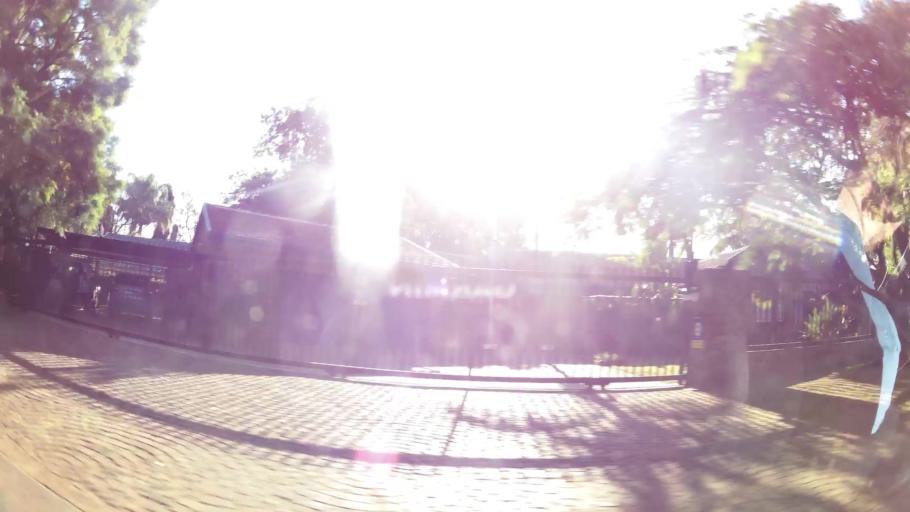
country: ZA
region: Gauteng
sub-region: City of Tshwane Metropolitan Municipality
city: Pretoria
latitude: -25.6778
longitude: 28.2288
